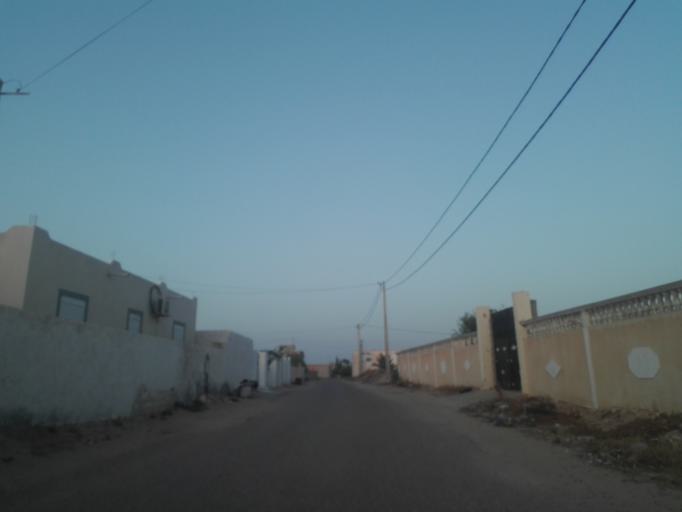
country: TN
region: Madanin
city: Houmt Souk
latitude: 33.7291
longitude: 10.7470
